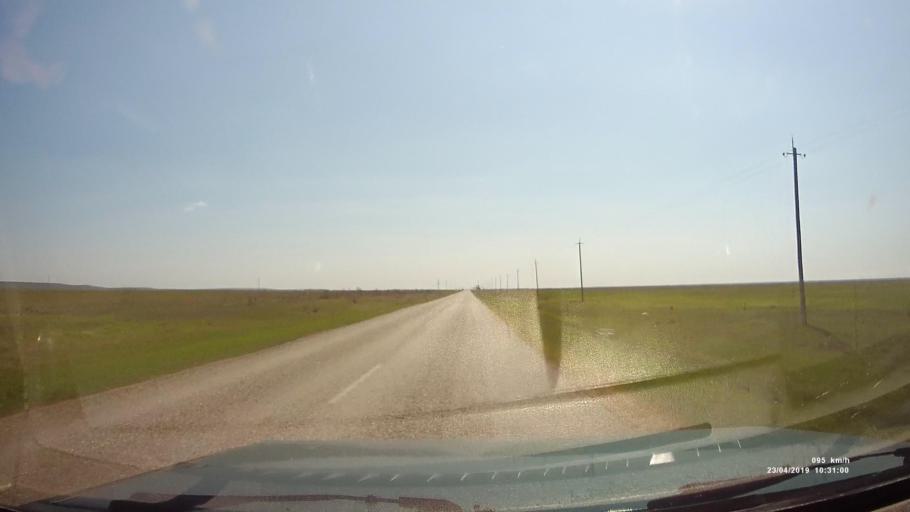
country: RU
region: Kalmykiya
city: Yashalta
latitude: 46.5885
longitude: 42.5547
